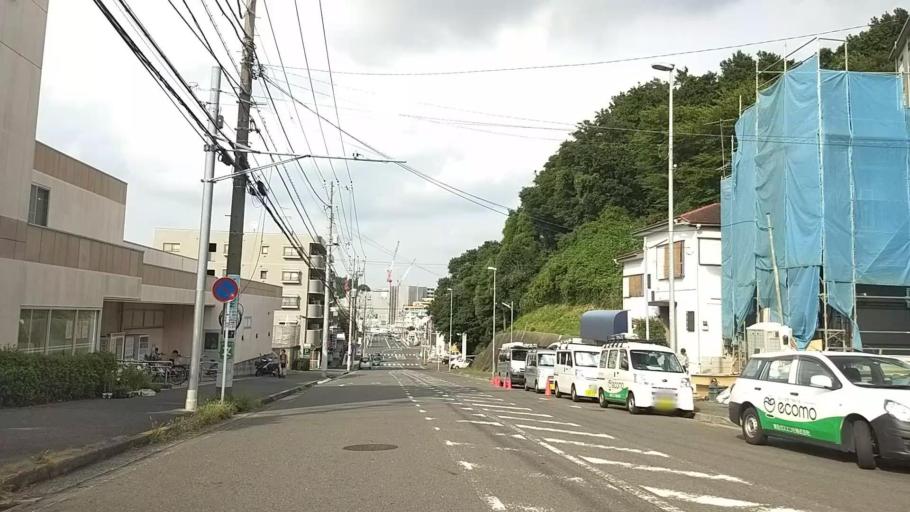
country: JP
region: Kanagawa
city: Yokohama
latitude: 35.5024
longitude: 139.5615
